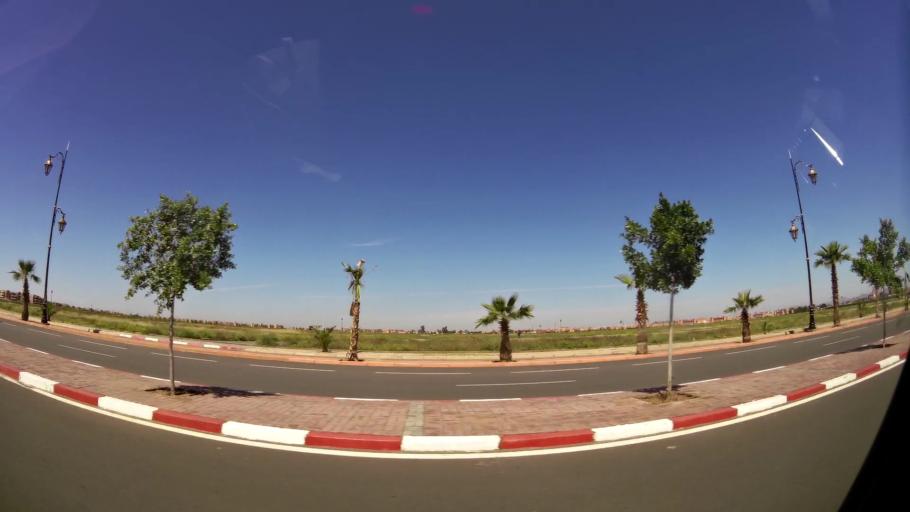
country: MA
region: Marrakech-Tensift-Al Haouz
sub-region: Marrakech
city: Marrakesh
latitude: 31.6025
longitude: -7.9896
